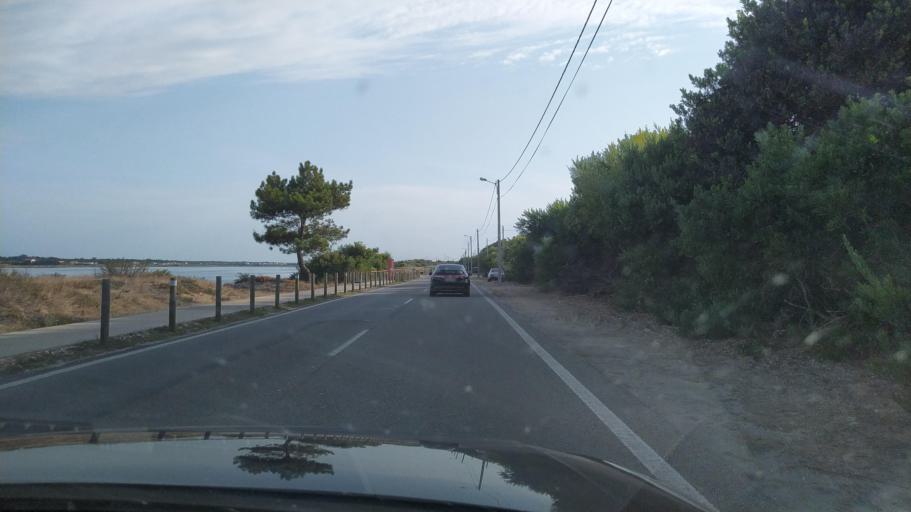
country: PT
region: Aveiro
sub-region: Ilhavo
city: Gafanha da Encarnacao
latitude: 40.5977
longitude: -8.7505
